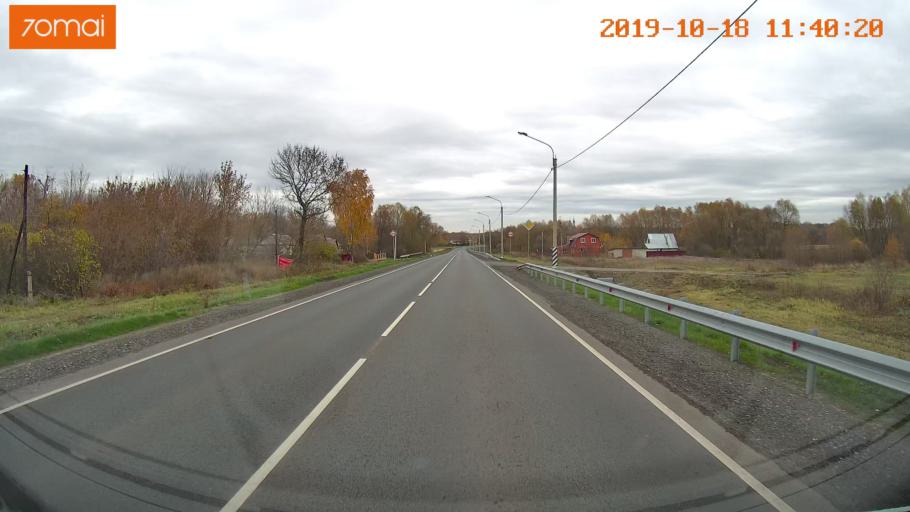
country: RU
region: Rjazan
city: Oktyabr'skiy
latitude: 54.1791
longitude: 38.8893
